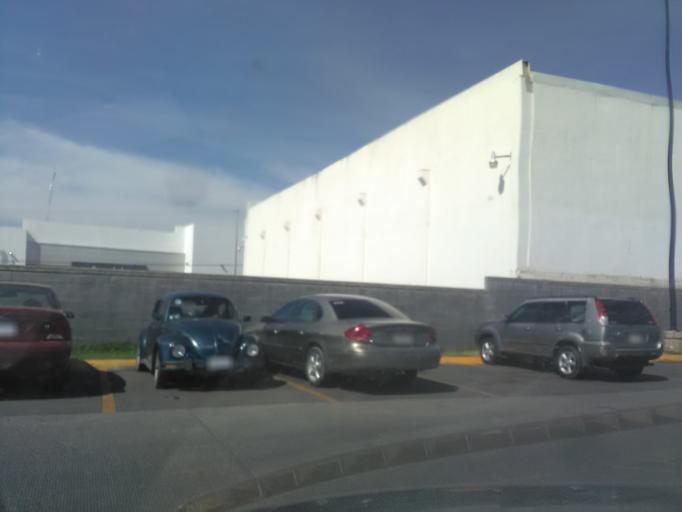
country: MX
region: Durango
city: Victoria de Durango
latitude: 24.0559
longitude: -104.6124
